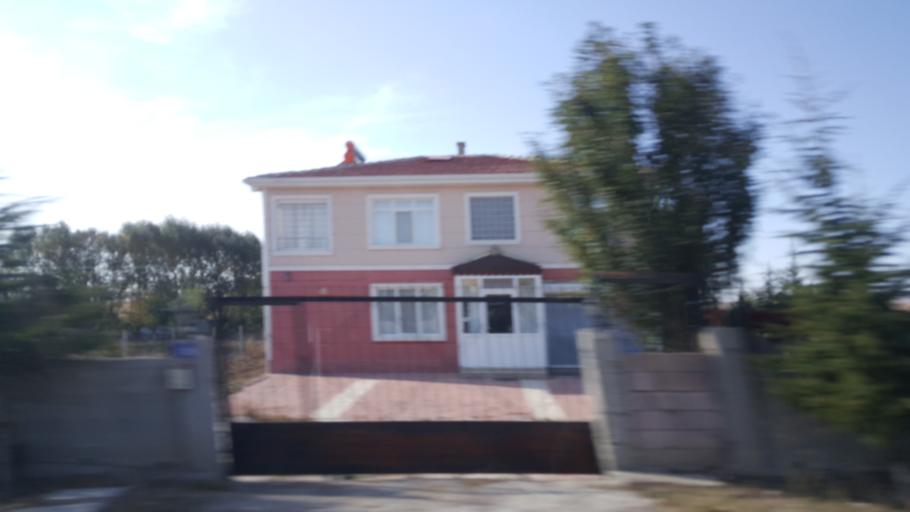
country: TR
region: Ankara
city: Yenice
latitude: 39.3663
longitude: 32.8105
